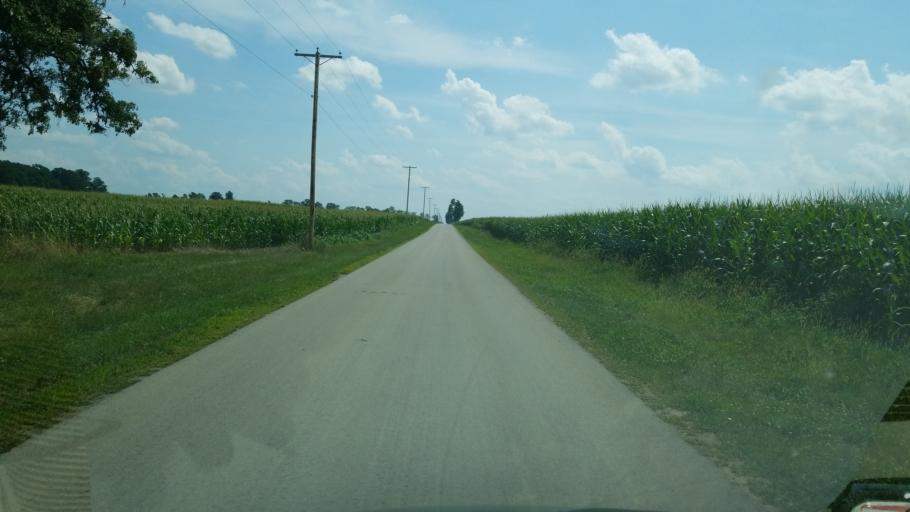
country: US
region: Ohio
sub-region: Hardin County
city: Forest
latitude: 40.8033
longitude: -83.4676
